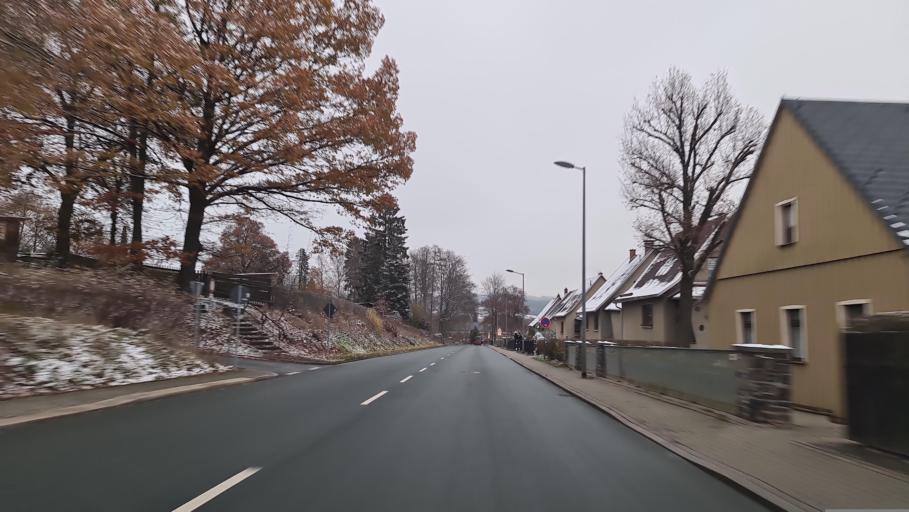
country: DE
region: Saxony
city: Markneukirchen
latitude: 50.3137
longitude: 12.3282
